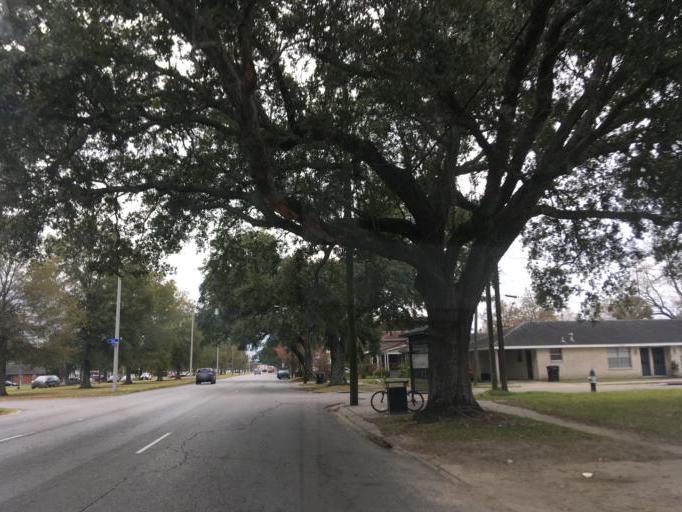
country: US
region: Louisiana
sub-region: Orleans Parish
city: New Orleans
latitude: 29.9952
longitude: -90.0591
